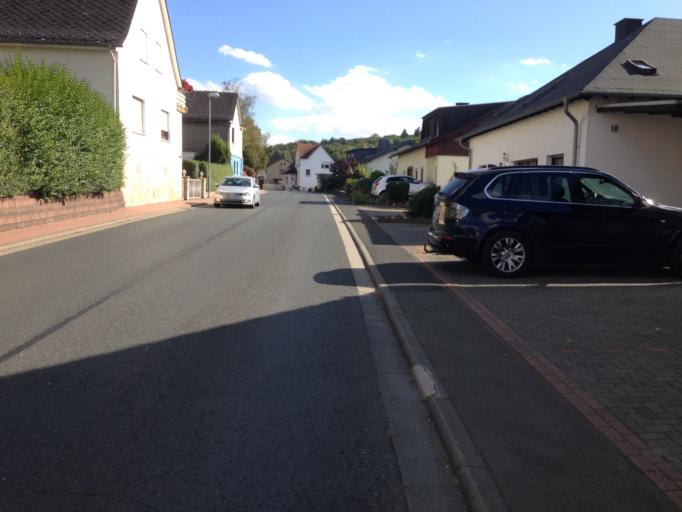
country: DE
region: Hesse
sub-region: Regierungsbezirk Giessen
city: Bischoffen
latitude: 50.6861
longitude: 8.4894
